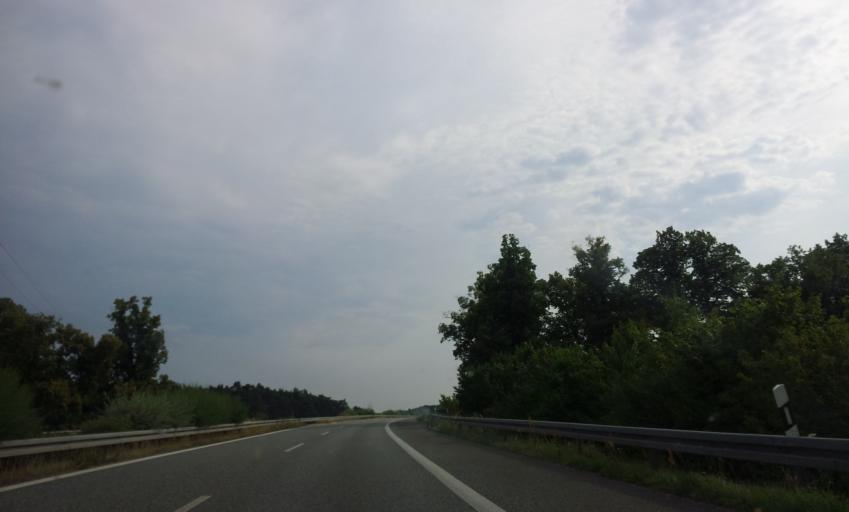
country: DE
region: Brandenburg
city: Ludwigsfelde
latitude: 52.2803
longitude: 13.2770
